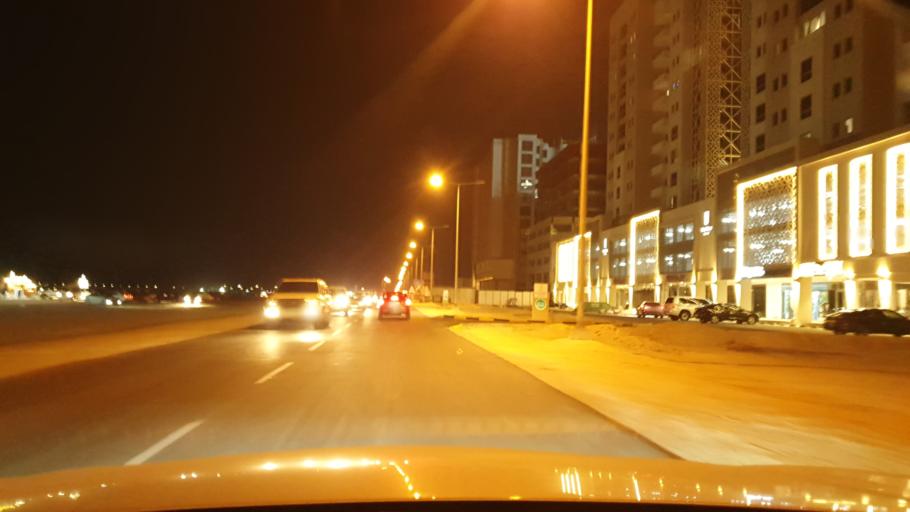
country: BH
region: Muharraq
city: Al Muharraq
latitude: 26.2631
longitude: 50.5945
